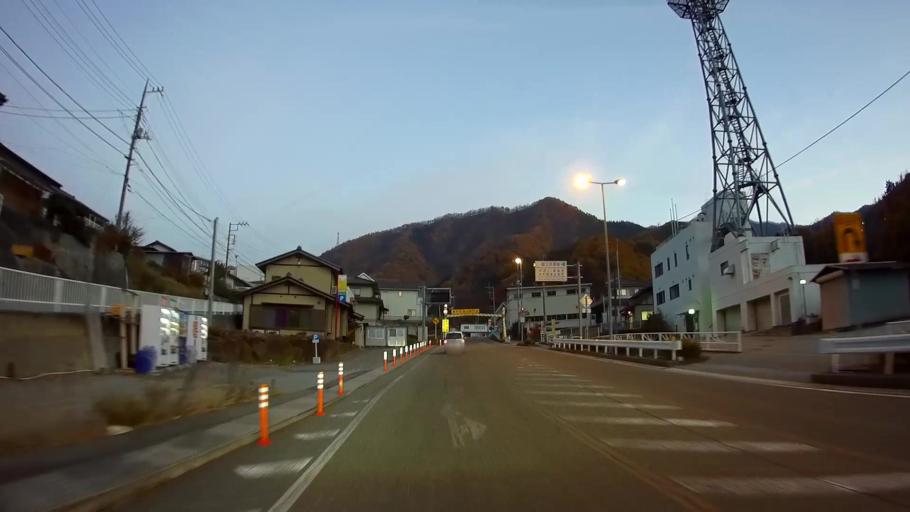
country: JP
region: Yamanashi
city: Enzan
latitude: 35.6403
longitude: 138.7757
